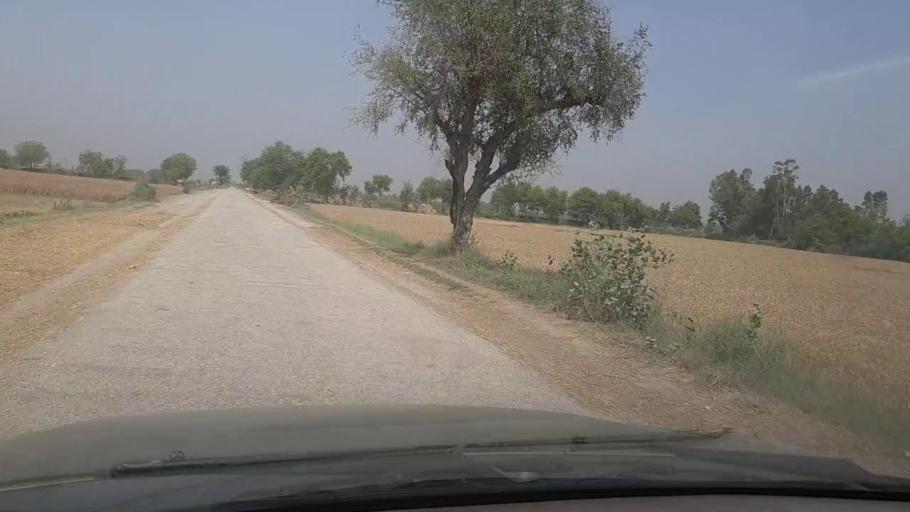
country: PK
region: Sindh
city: Madeji
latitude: 27.7957
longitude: 68.4717
